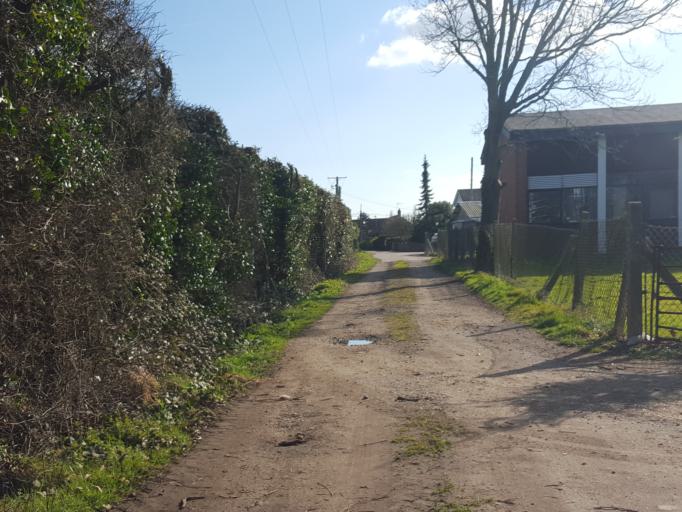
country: GB
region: England
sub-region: Essex
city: Little Clacton
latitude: 51.8606
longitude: 1.1147
